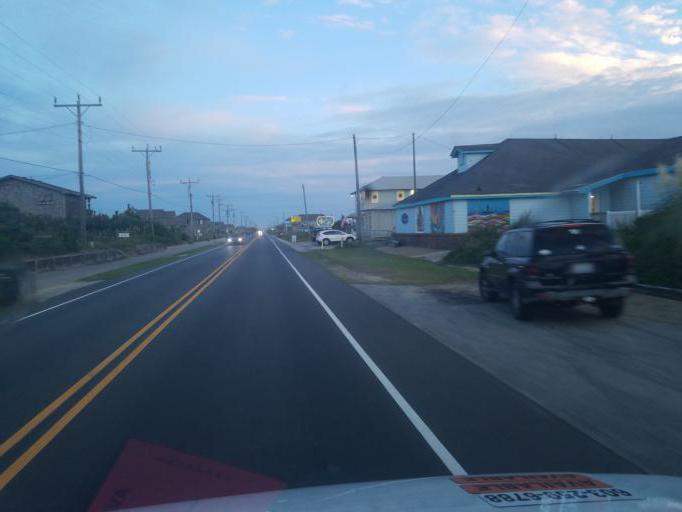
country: US
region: North Carolina
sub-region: Dare County
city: Nags Head
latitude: 35.9585
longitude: -75.6248
